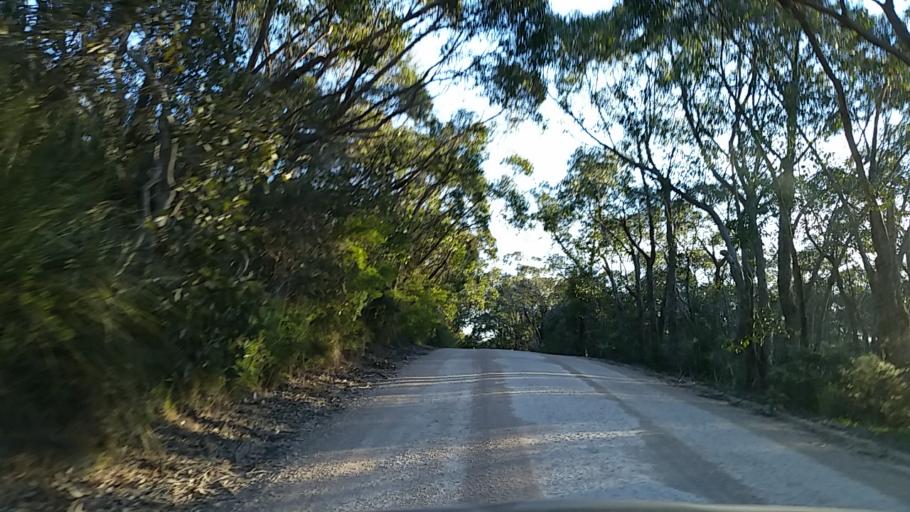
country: AU
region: South Australia
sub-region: Alexandrina
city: Mount Compass
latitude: -35.3024
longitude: 138.6787
